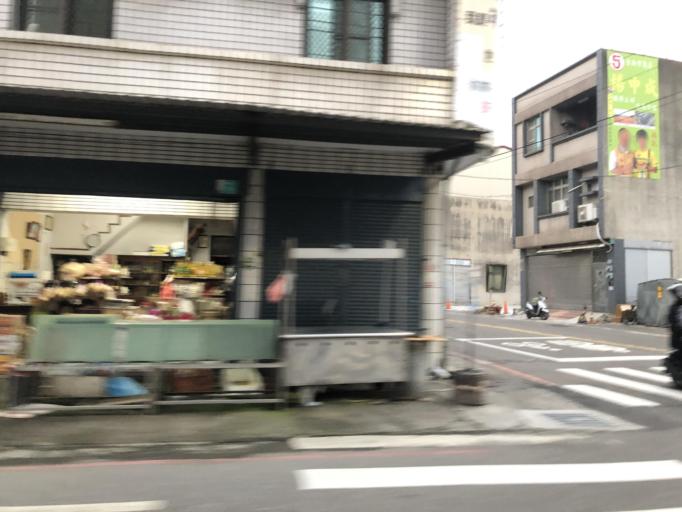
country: TW
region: Taiwan
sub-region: Tainan
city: Tainan
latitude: 23.0208
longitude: 120.2790
